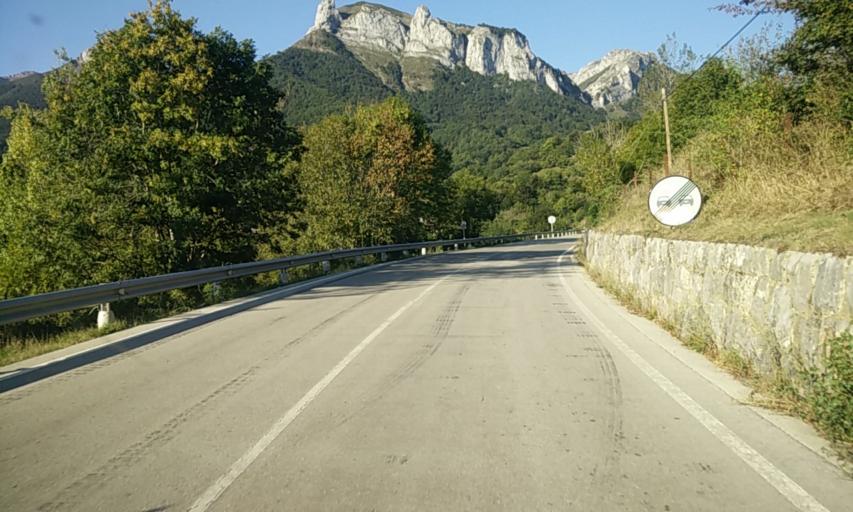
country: ES
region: Cantabria
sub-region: Provincia de Cantabria
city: Camaleno
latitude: 43.1307
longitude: -4.8018
